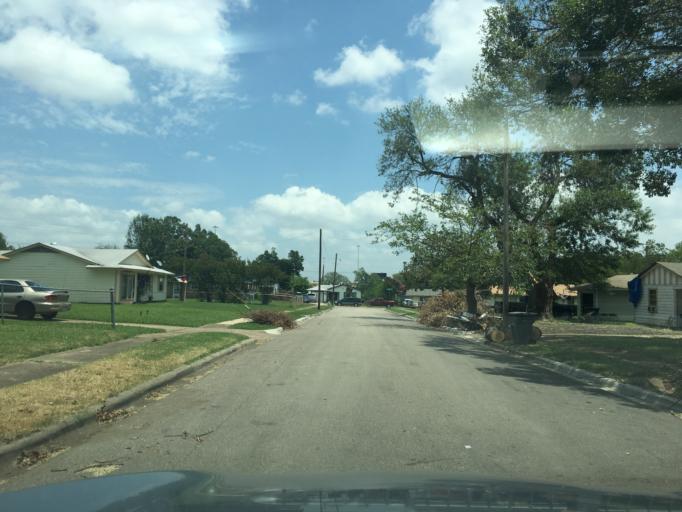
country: US
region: Texas
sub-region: Dallas County
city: Richardson
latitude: 32.9200
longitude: -96.7563
